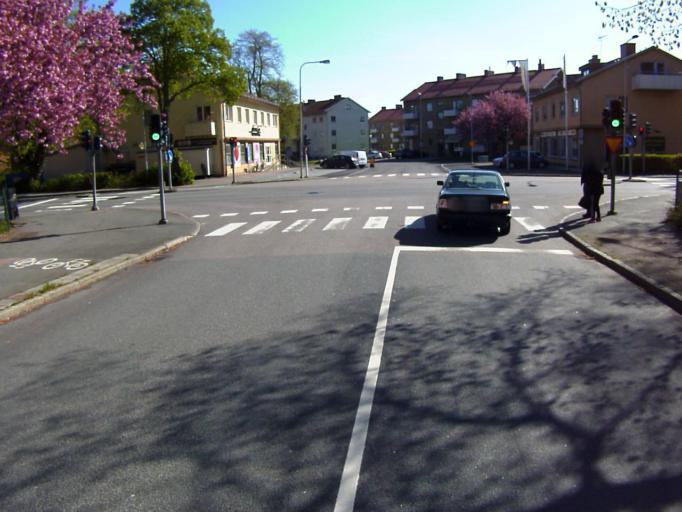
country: SE
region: Skane
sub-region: Kristianstads Kommun
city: Kristianstad
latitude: 56.0336
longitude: 14.1655
